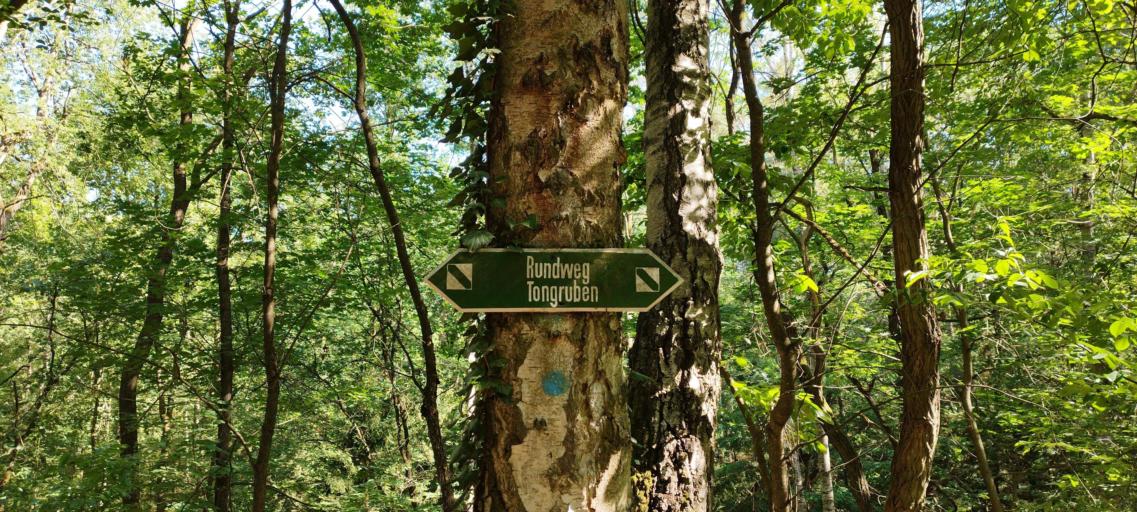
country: DE
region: Brandenburg
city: Reichenwalde
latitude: 52.2866
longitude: 14.0303
